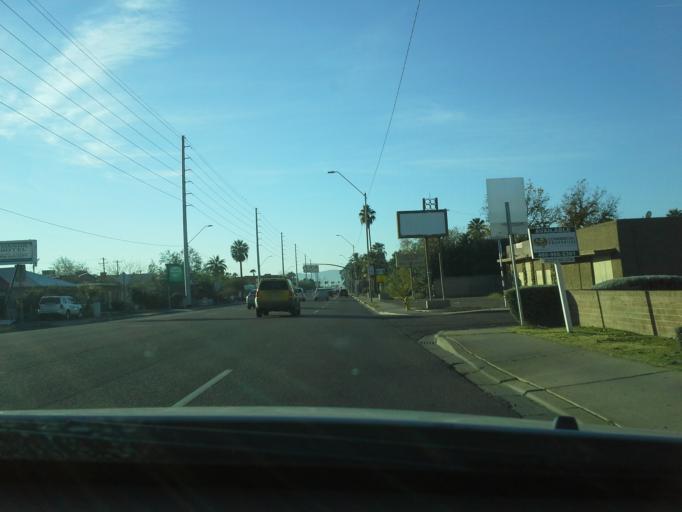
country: US
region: Arizona
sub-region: Maricopa County
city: Phoenix
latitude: 33.4728
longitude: -112.0652
